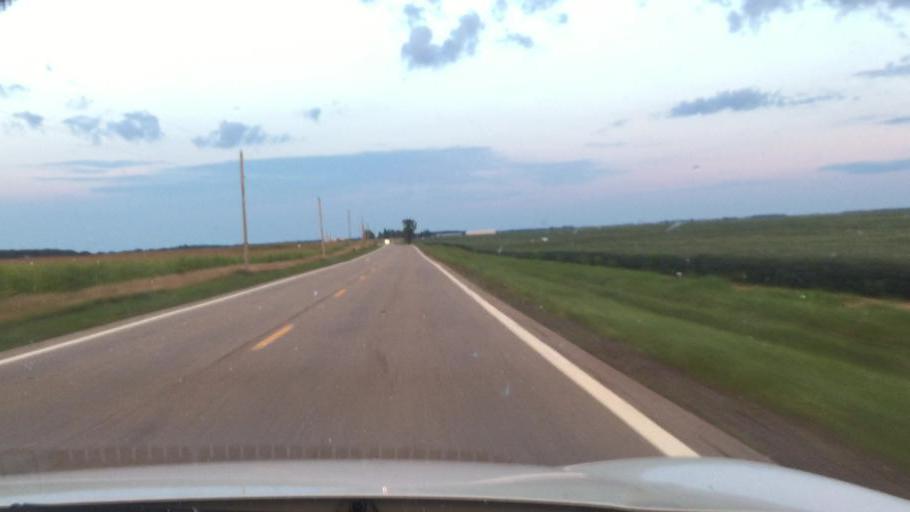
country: US
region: Ohio
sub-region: Madison County
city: Choctaw Lake
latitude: 40.0112
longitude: -83.4537
